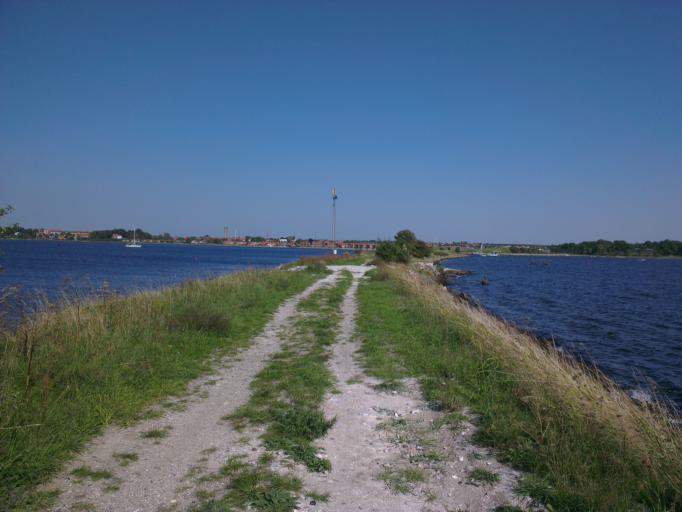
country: DK
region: Capital Region
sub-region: Frederikssund Kommune
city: Frederikssund
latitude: 55.8317
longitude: 12.0420
